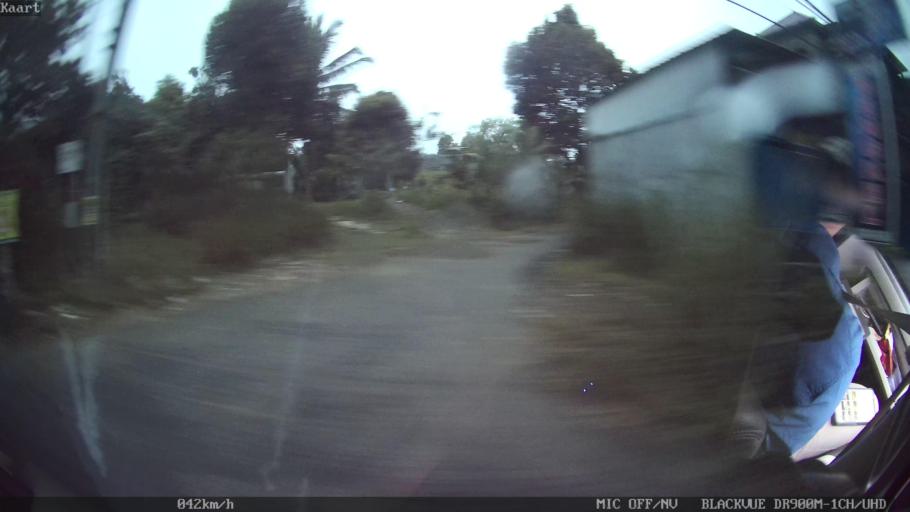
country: ID
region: Bali
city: Banjar Taro Kelod
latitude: -8.3141
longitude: 115.3013
